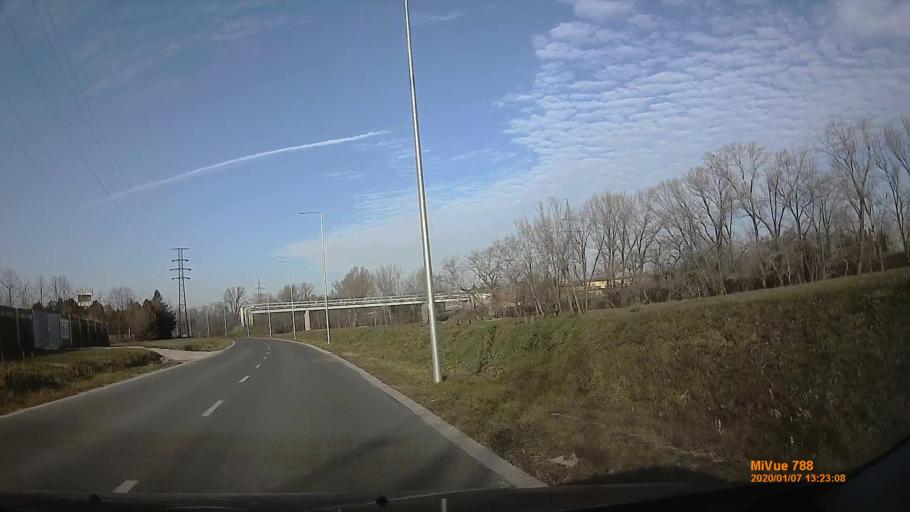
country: HU
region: Gyor-Moson-Sopron
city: Gyor
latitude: 47.6928
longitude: 17.6730
